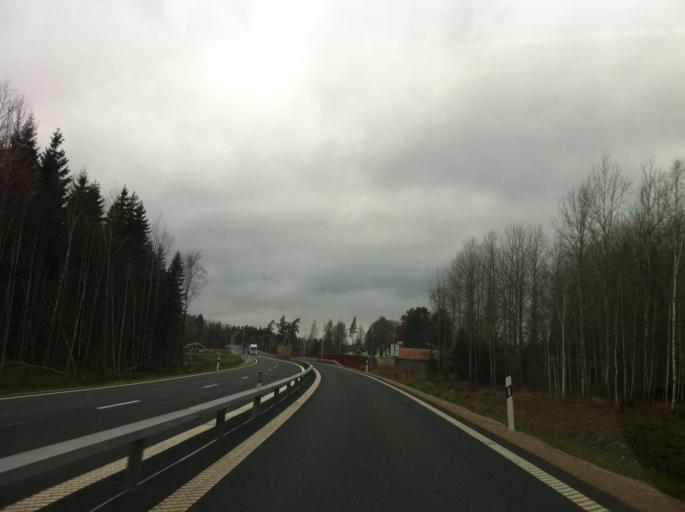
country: SE
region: Joenkoeping
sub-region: Vetlanda Kommun
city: Vetlanda
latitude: 57.4306
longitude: 15.1781
